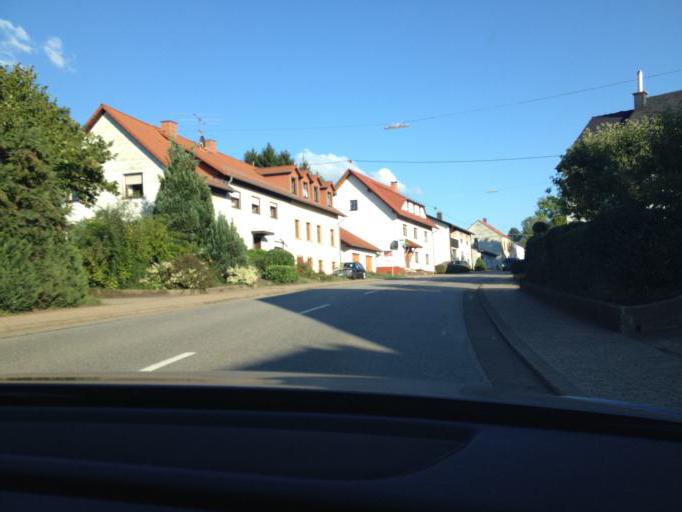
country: DE
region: Saarland
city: Tholey
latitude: 49.4990
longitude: 7.0275
